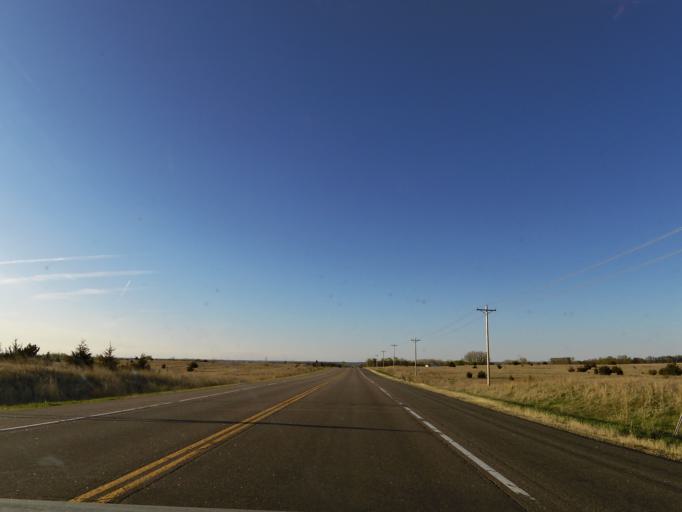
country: US
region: Wisconsin
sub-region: Pierce County
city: Prescott
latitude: 44.6305
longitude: -92.7723
